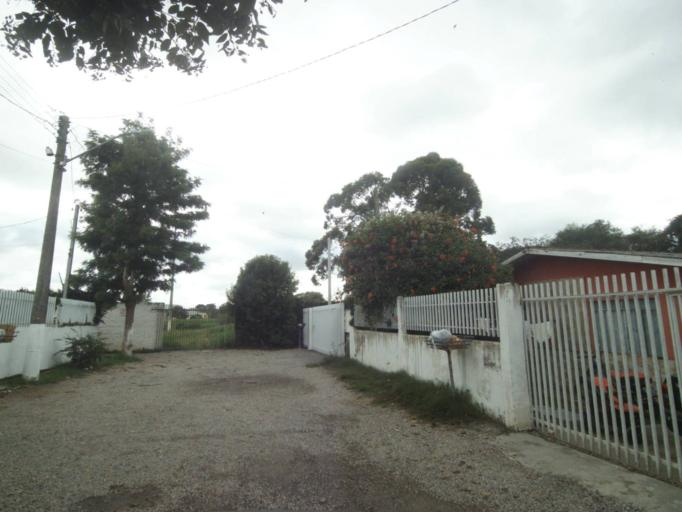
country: BR
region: Parana
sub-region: Pinhais
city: Pinhais
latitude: -25.4605
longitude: -49.1928
